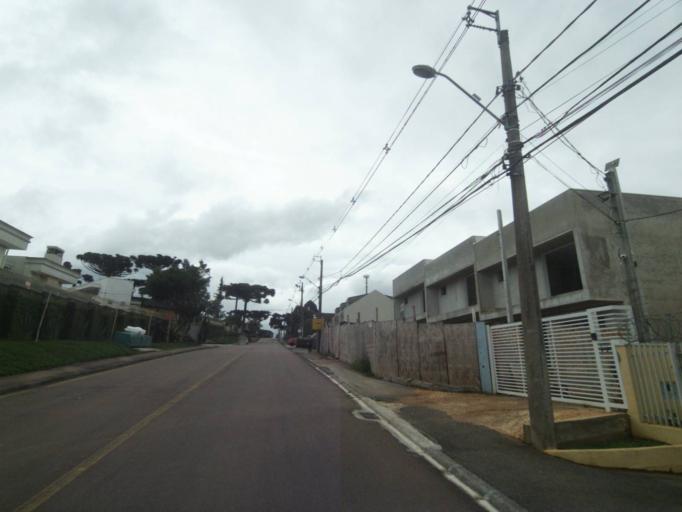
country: BR
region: Parana
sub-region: Curitiba
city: Curitiba
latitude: -25.4587
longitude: -49.3368
